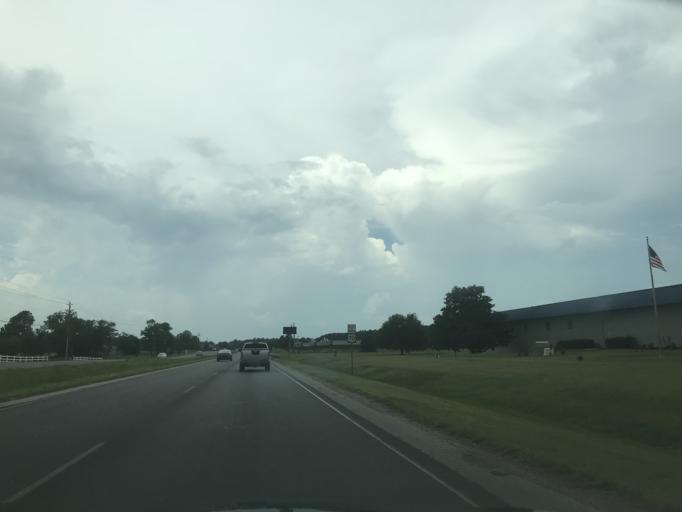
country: US
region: North Carolina
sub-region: Johnston County
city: Clayton
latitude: 35.6239
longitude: -78.4247
